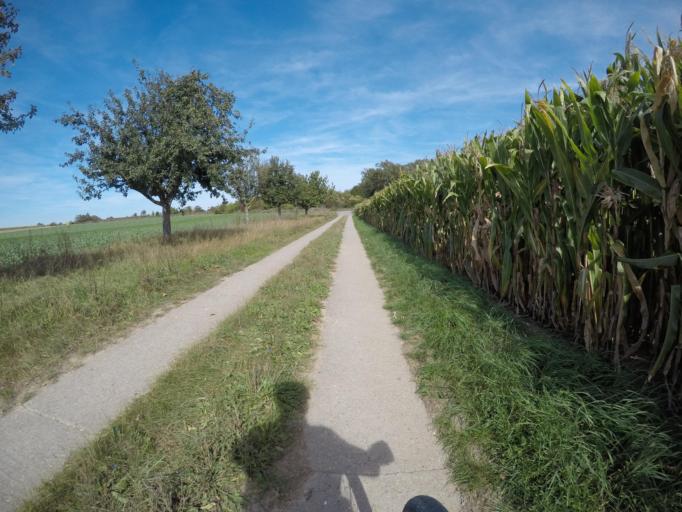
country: DE
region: Baden-Wuerttemberg
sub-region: Regierungsbezirk Stuttgart
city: Sersheim
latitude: 48.9492
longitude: 9.0249
